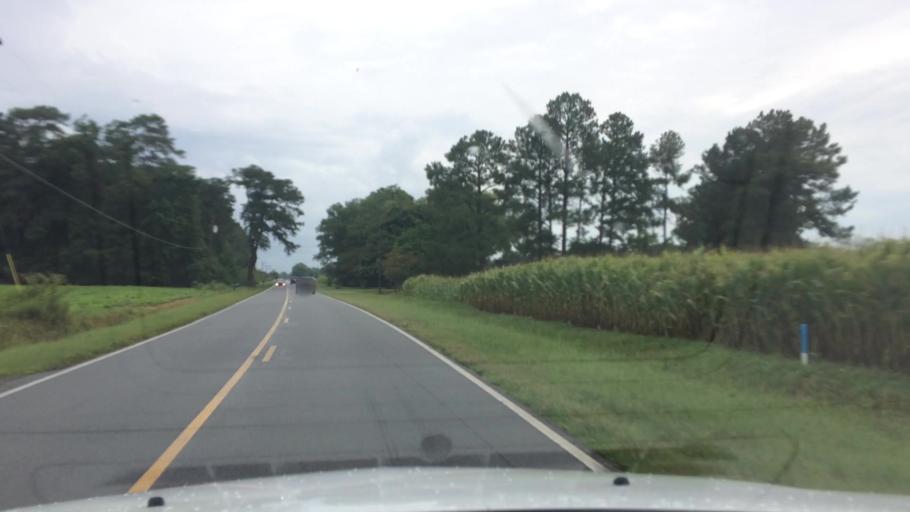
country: US
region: North Carolina
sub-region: Pitt County
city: Farmville
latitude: 35.5543
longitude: -77.5450
